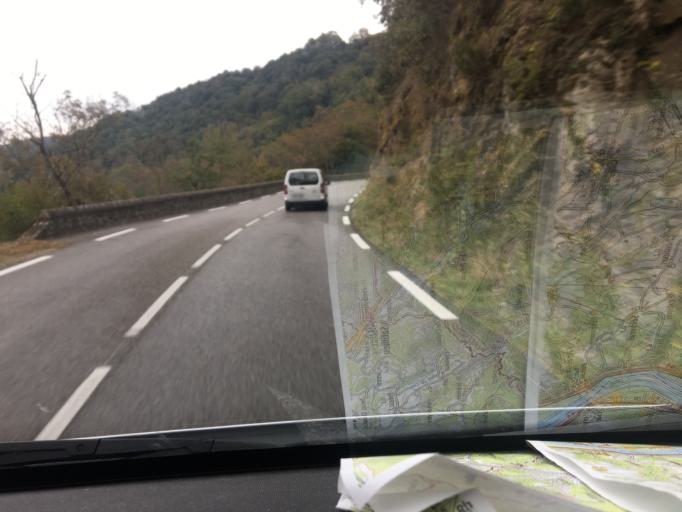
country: FR
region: Rhone-Alpes
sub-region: Departement de l'Ardeche
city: Saint-Jean-de-Muzols
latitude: 45.0569
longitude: 4.7697
